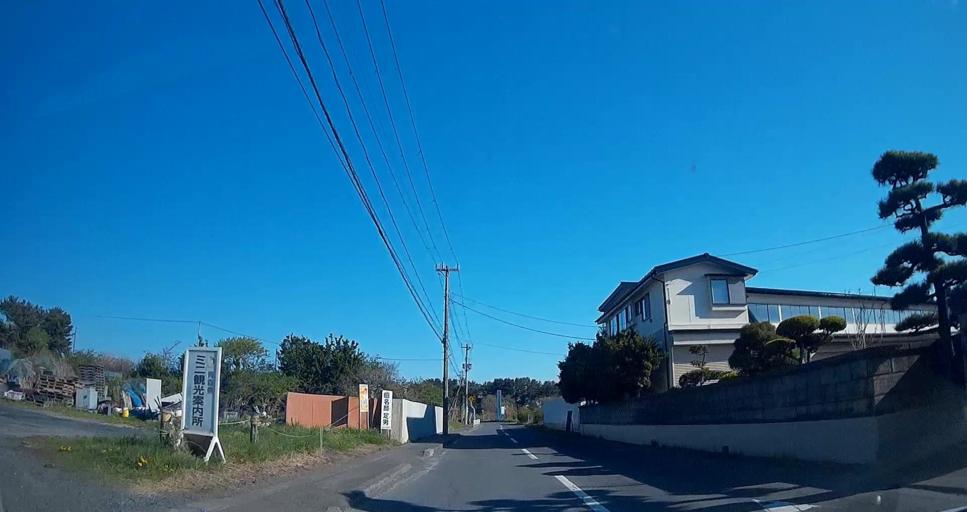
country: JP
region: Aomori
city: Hachinohe
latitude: 40.5113
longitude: 141.6070
